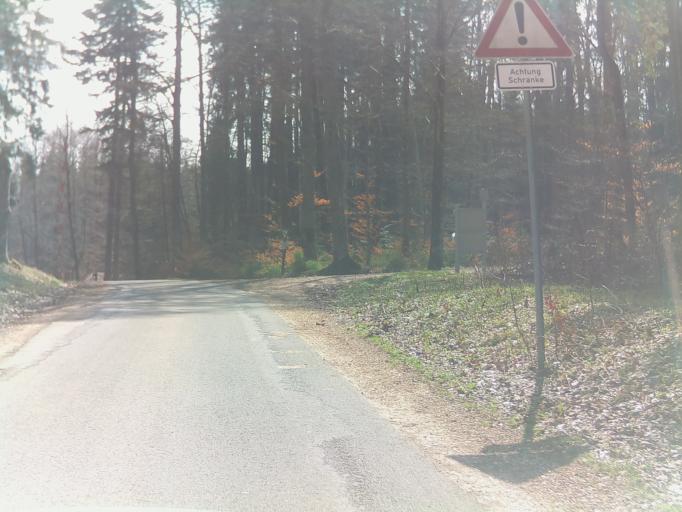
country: DE
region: Baden-Wuerttemberg
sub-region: Tuebingen Region
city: Gomadingen
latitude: 48.4368
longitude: 9.4232
